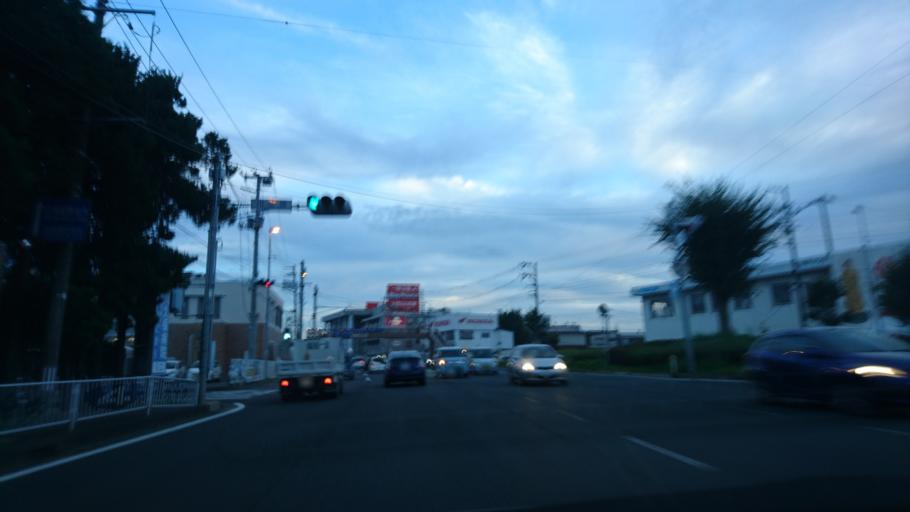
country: JP
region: Iwate
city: Morioka-shi
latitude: 39.6731
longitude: 141.1555
